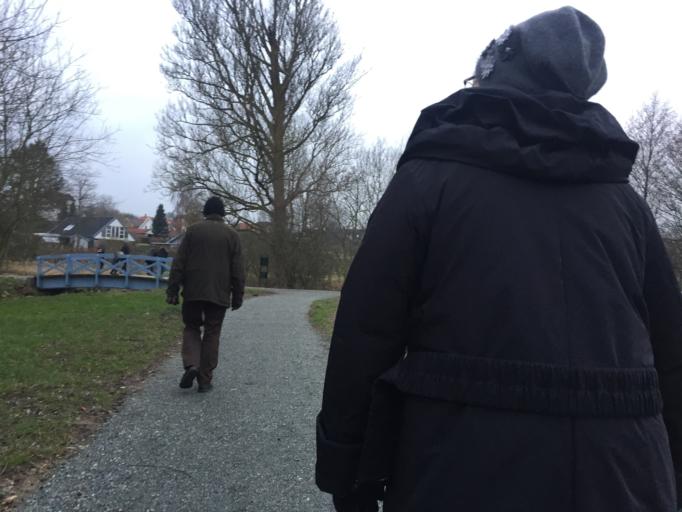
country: DK
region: South Denmark
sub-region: Kolding Kommune
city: Sonder Bjert
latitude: 55.4562
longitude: 9.5610
